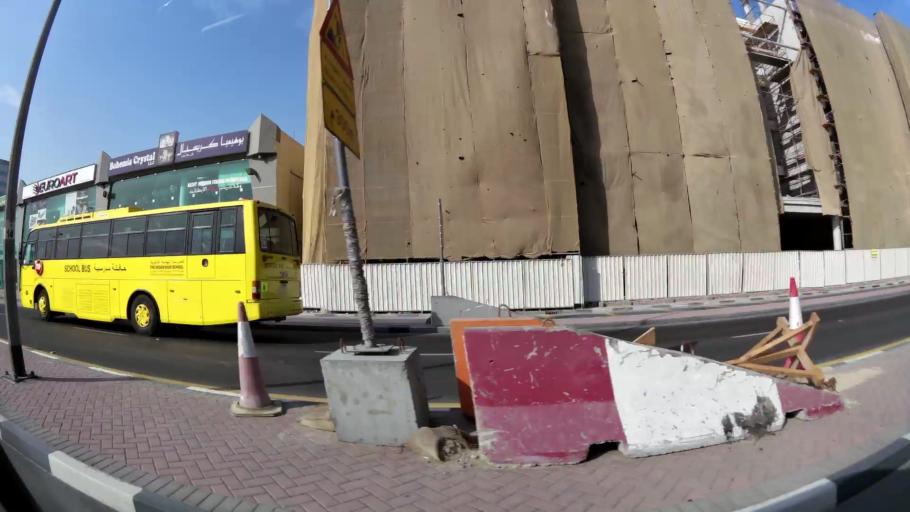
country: AE
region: Ash Shariqah
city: Sharjah
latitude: 25.2525
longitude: 55.3435
